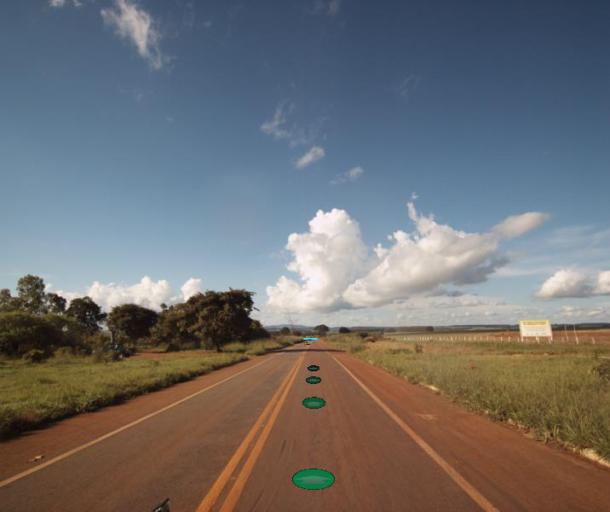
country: BR
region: Goias
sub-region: Itaberai
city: Itaberai
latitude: -16.0253
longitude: -49.7775
